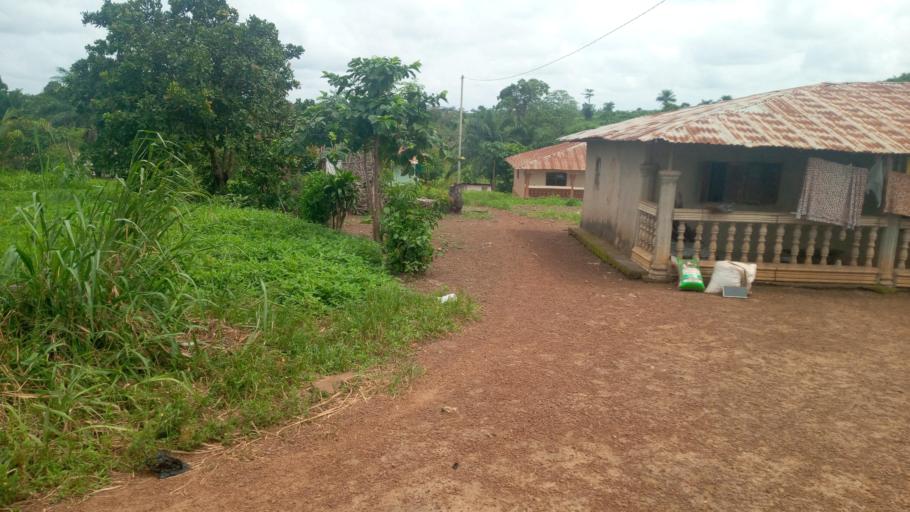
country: SL
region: Southern Province
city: Mogbwemo
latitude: 7.7769
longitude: -12.3033
